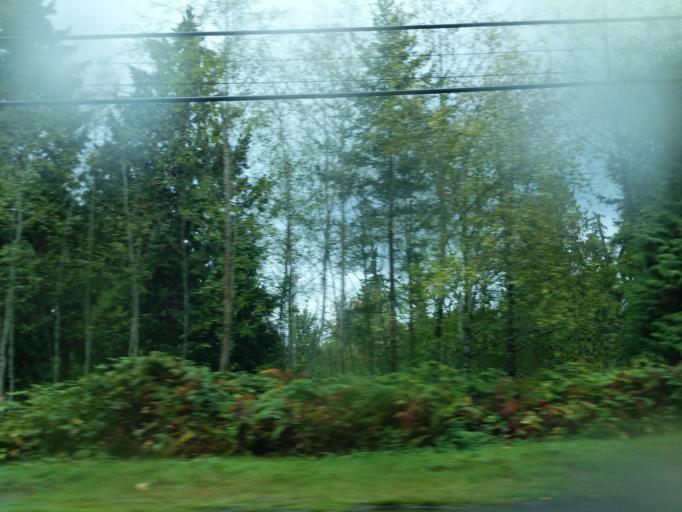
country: US
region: Washington
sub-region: King County
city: Bothell
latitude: 47.7842
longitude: -122.2073
